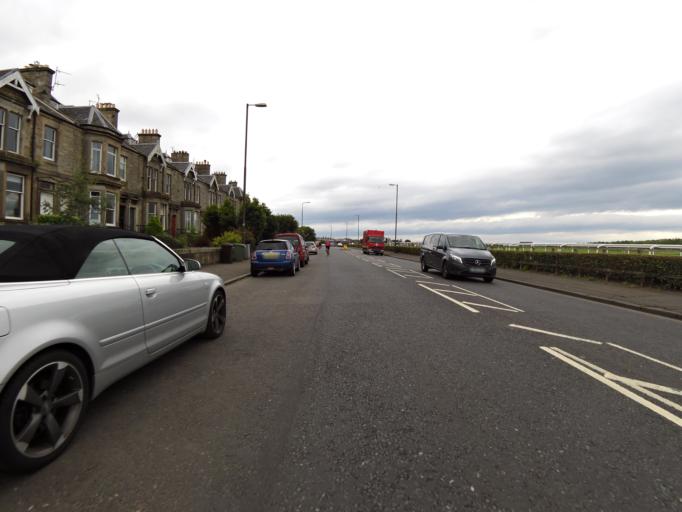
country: GB
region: Scotland
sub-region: East Lothian
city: Musselburgh
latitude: 55.9456
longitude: -3.0359
